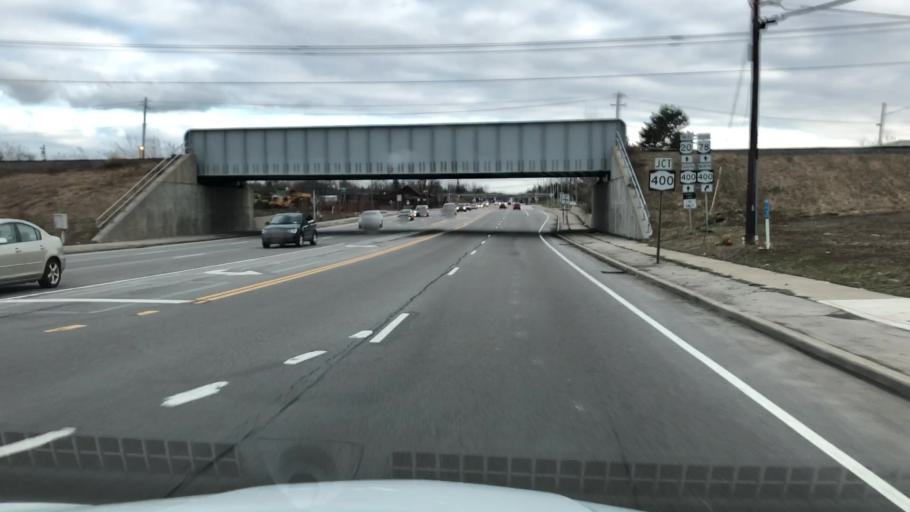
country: US
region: New York
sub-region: Erie County
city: Elma Center
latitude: 42.8389
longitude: -78.6970
